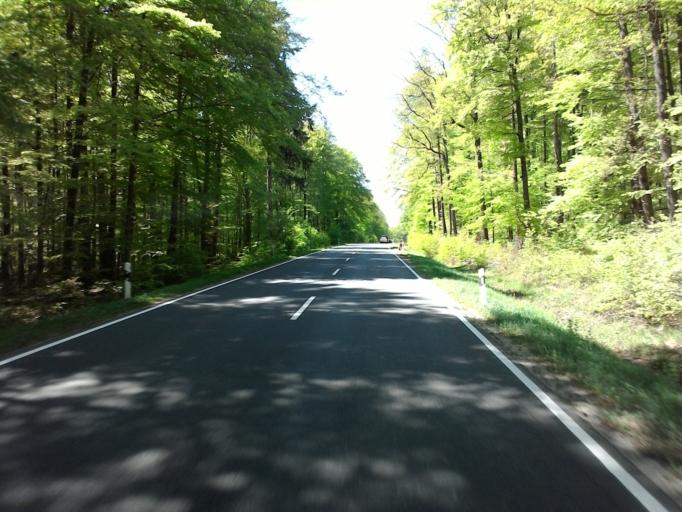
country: DE
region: Bavaria
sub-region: Regierungsbezirk Unterfranken
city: Neuhutten
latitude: 49.9781
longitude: 9.4507
